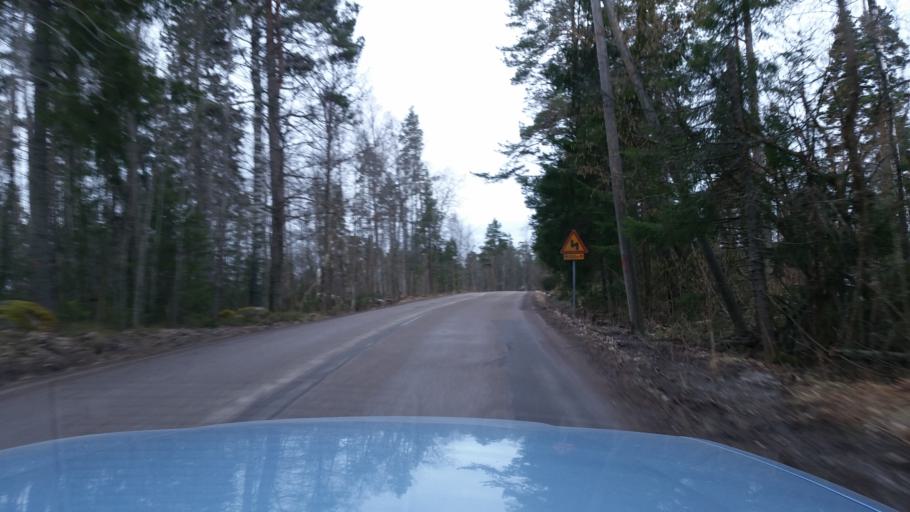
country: FI
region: Uusimaa
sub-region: Helsinki
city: Kauniainen
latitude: 60.2649
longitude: 24.6910
